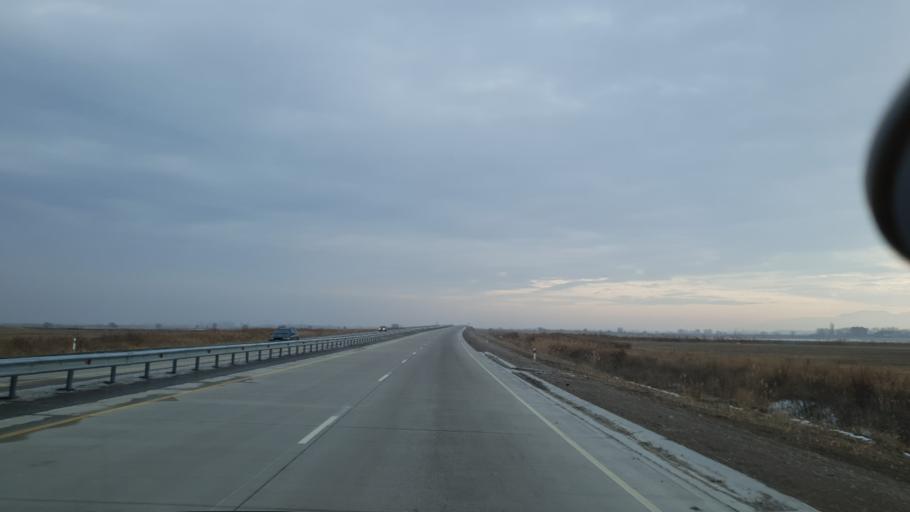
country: KZ
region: Almaty Oblysy
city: Talghar
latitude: 43.4669
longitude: 77.2887
